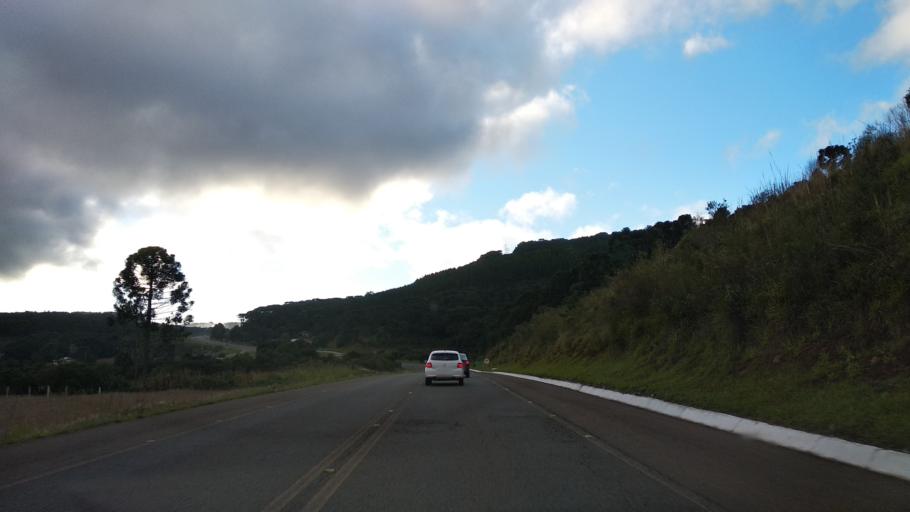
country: BR
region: Santa Catarina
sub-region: Curitibanos
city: Curitibanos
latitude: -27.5780
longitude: -50.7757
